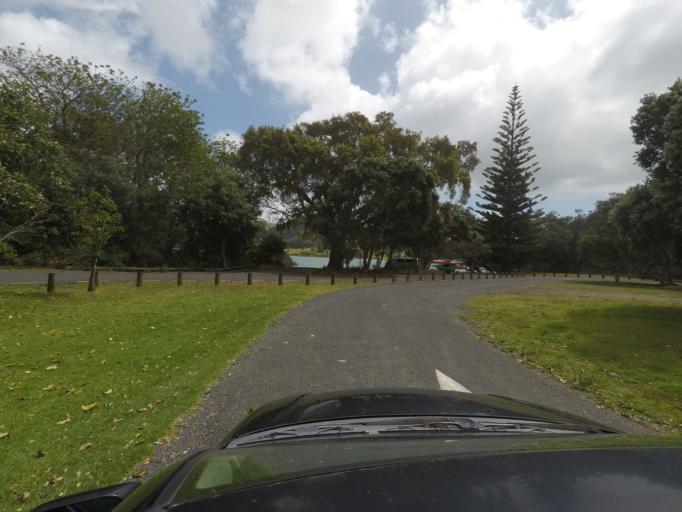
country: NZ
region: Auckland
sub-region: Auckland
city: Warkworth
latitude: -36.5318
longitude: 174.7110
